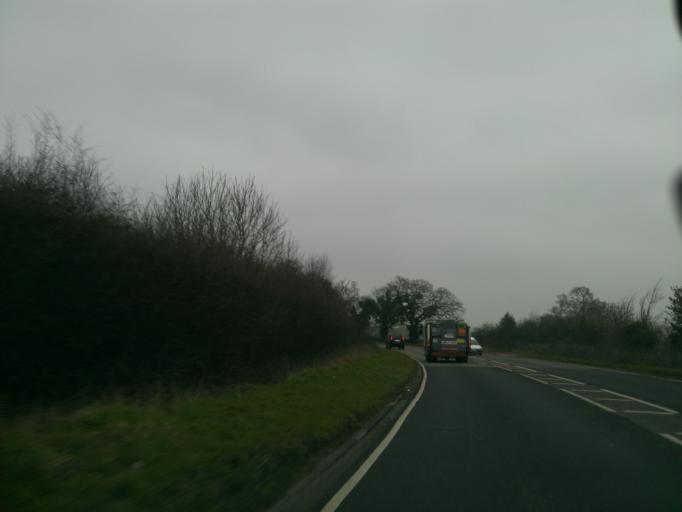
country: GB
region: England
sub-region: Essex
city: Great Bentley
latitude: 51.8646
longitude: 1.0815
